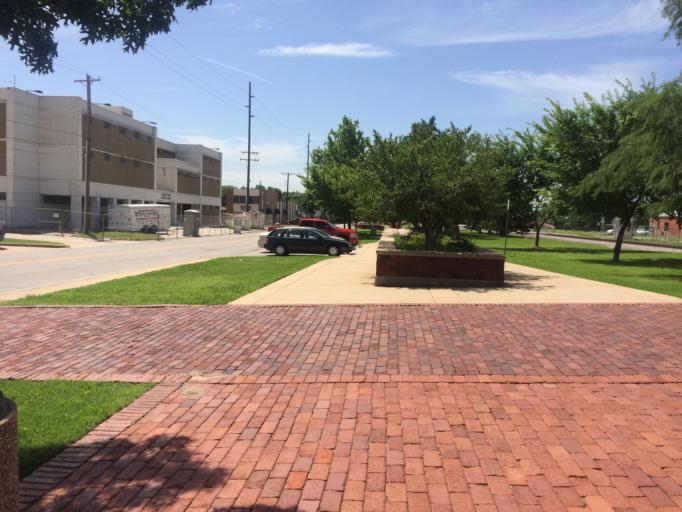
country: US
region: Oklahoma
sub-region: Cleveland County
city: Norman
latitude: 35.2198
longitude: -97.4428
